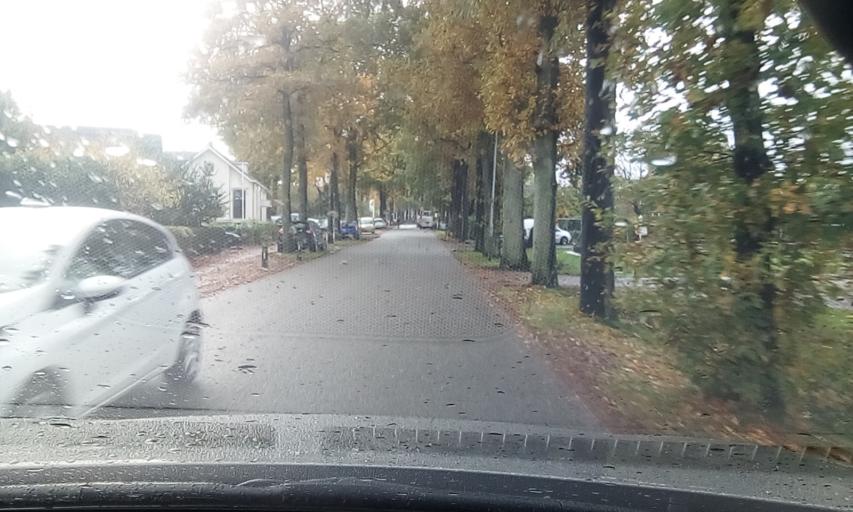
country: NL
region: Groningen
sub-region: Gemeente Hoogezand-Sappemeer
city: Hoogezand
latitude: 53.2058
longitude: 6.7070
